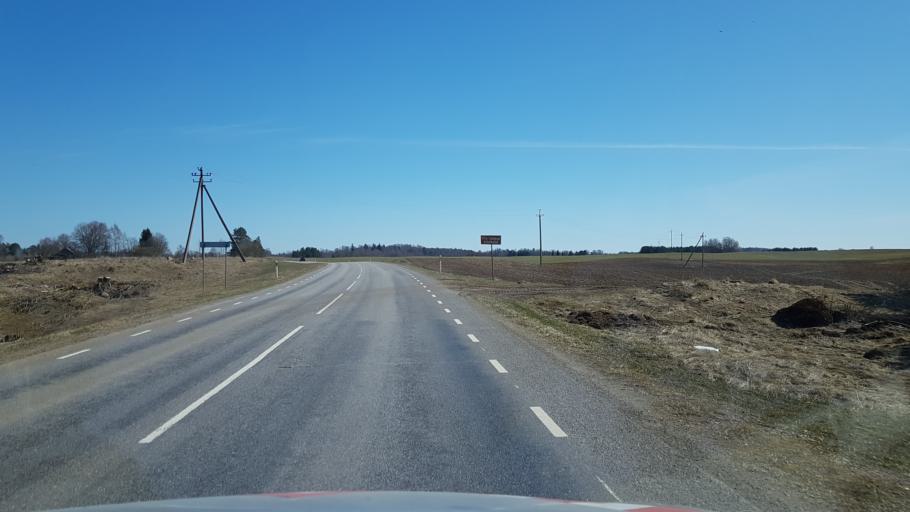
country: EE
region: Laeaene-Virumaa
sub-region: Vinni vald
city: Vinni
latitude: 59.3175
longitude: 26.4402
